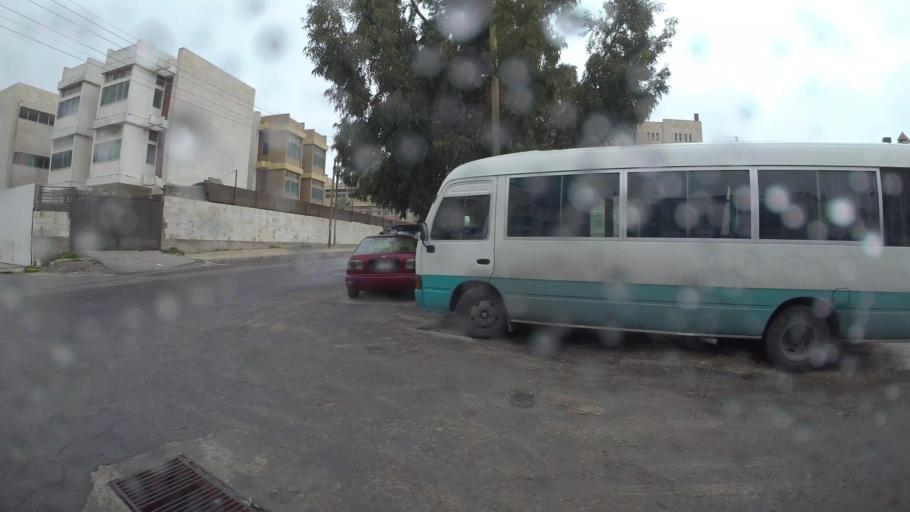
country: JO
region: Amman
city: Al Jubayhah
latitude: 31.9896
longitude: 35.8659
